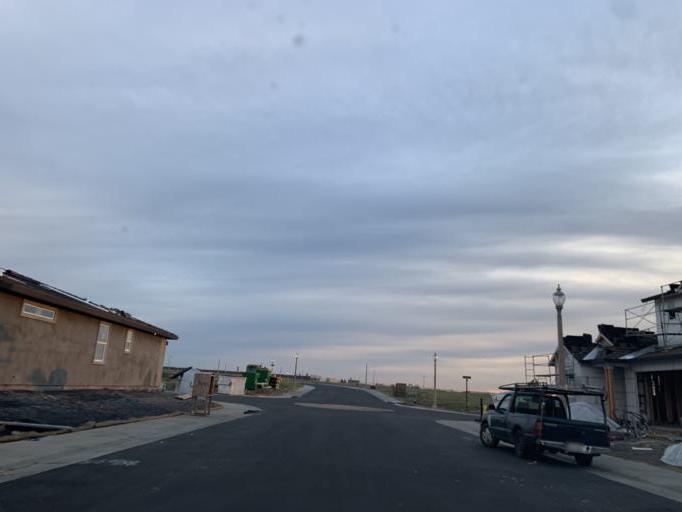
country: US
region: California
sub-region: Placer County
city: Lincoln
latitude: 38.8588
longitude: -121.2920
